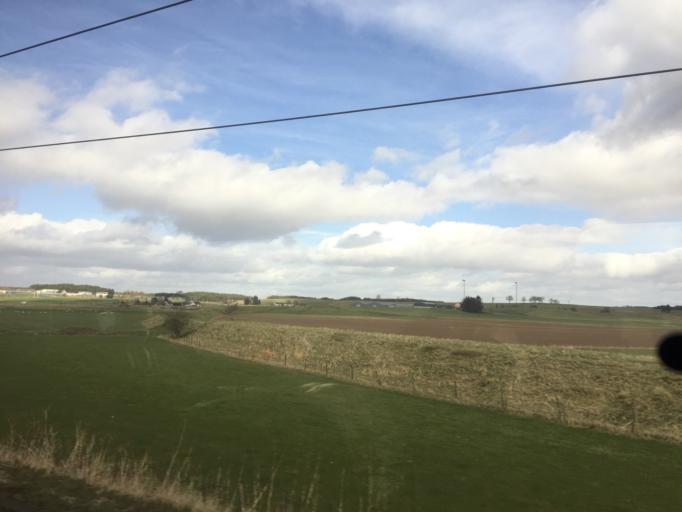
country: GB
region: Scotland
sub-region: South Lanarkshire
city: Carnwath
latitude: 55.6825
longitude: -3.6545
